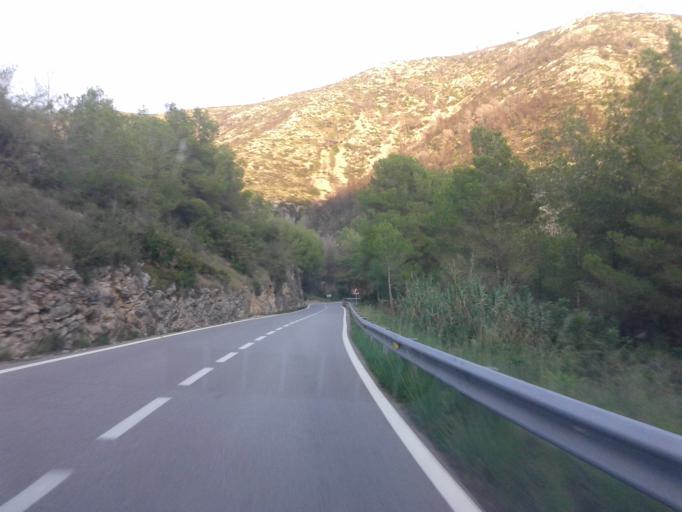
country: ES
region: Catalonia
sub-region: Provincia de Barcelona
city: Castellet
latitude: 41.2468
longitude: 1.6620
